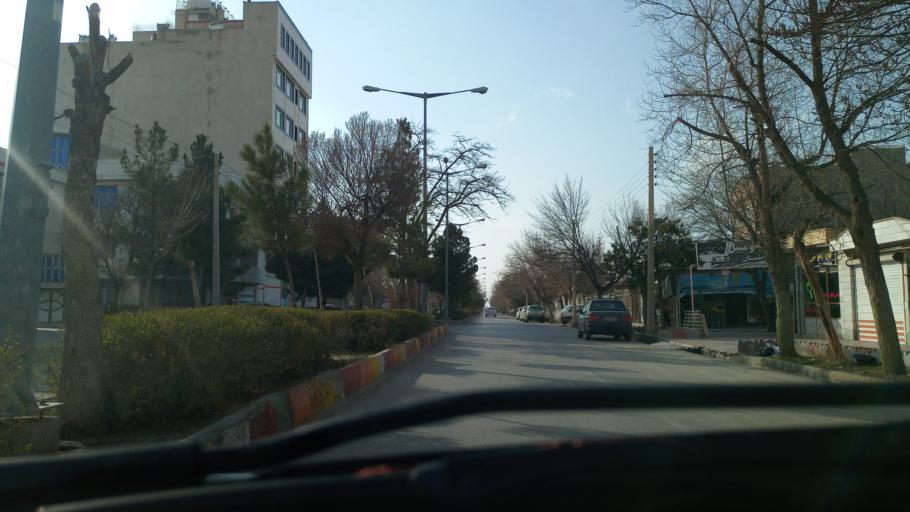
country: IR
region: Razavi Khorasan
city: Quchan
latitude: 37.0991
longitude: 58.5026
